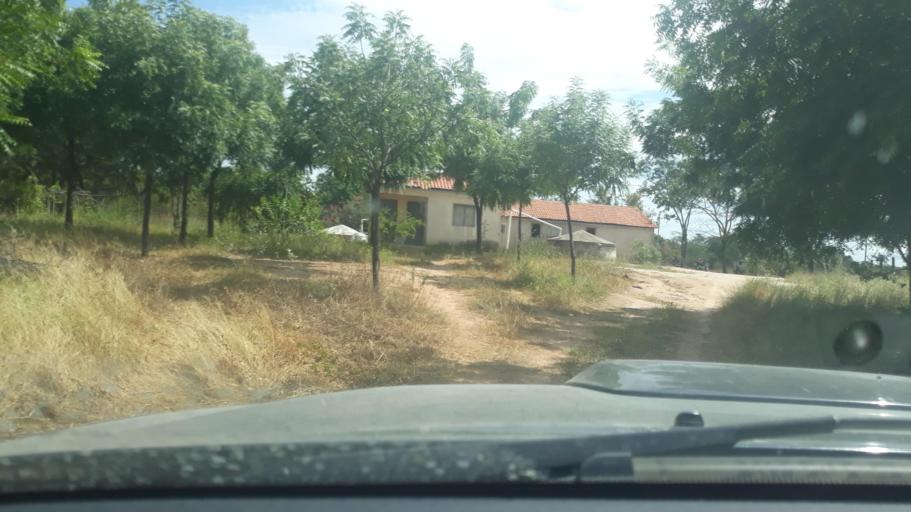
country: BR
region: Bahia
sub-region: Riacho De Santana
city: Riacho de Santana
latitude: -13.8665
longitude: -43.0778
